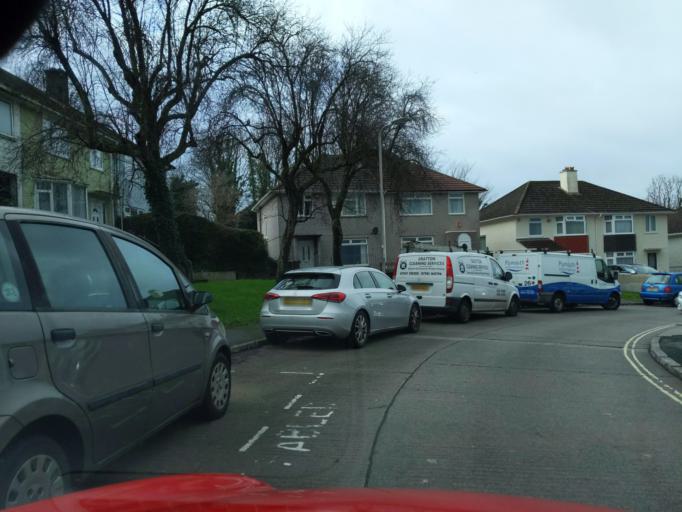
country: GB
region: England
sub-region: Plymouth
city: Plymouth
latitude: 50.3987
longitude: -4.1575
